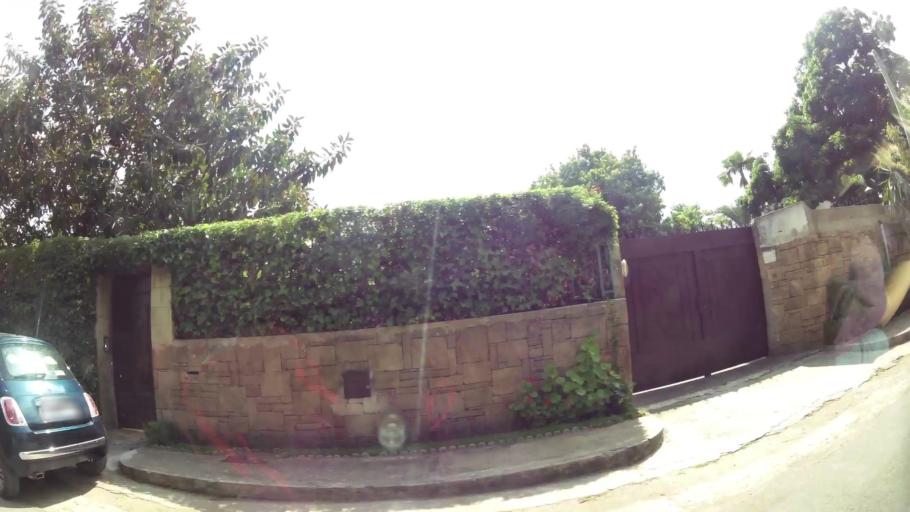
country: MA
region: Rabat-Sale-Zemmour-Zaer
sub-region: Rabat
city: Rabat
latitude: 33.9822
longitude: -6.8379
